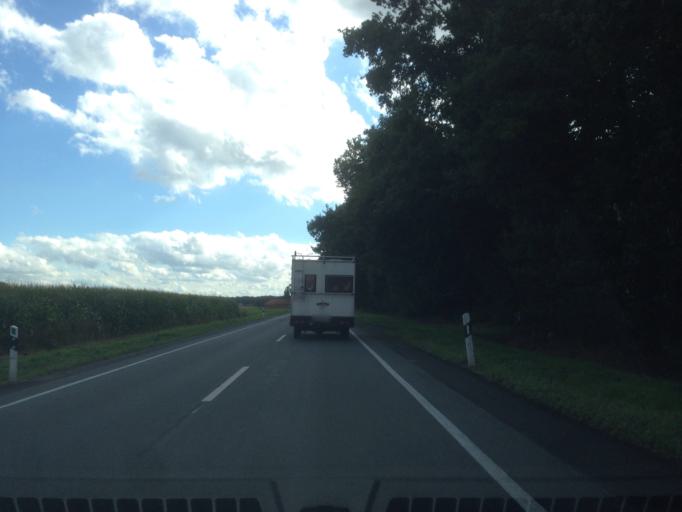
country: DE
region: North Rhine-Westphalia
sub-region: Regierungsbezirk Munster
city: Senden
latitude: 51.8631
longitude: 7.5483
